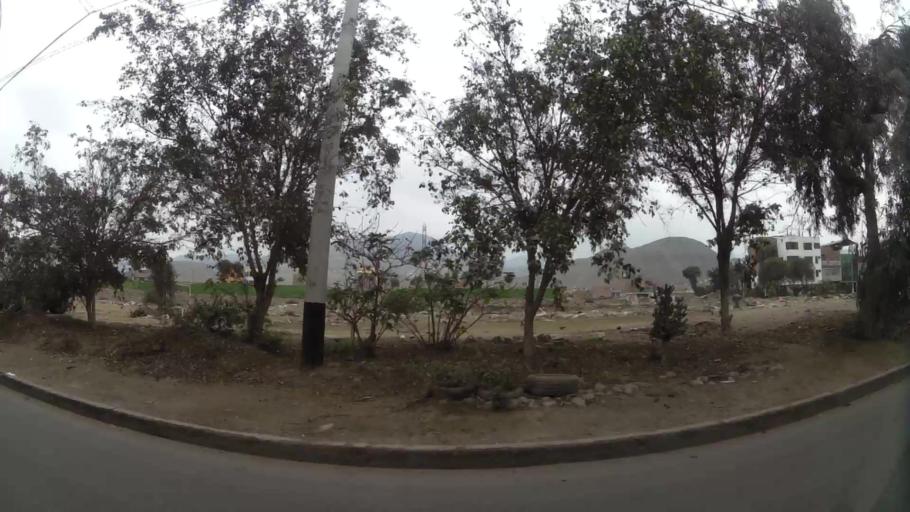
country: PE
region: Lima
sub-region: Lima
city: Independencia
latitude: -11.9335
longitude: -77.0808
